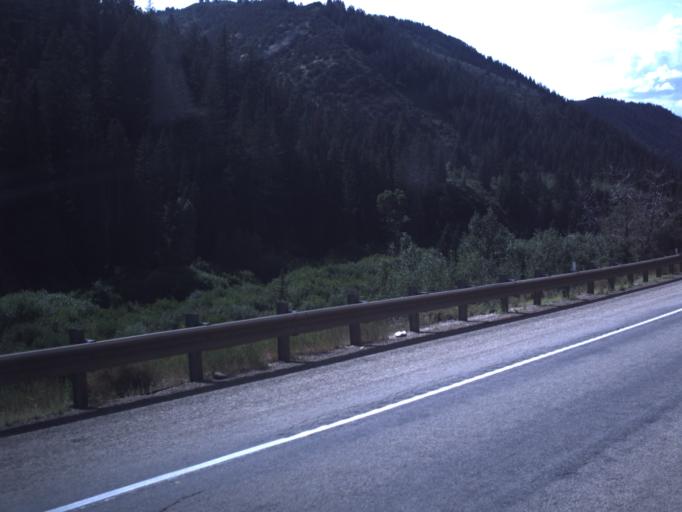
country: US
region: Utah
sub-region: Wasatch County
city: Heber
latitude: 40.3445
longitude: -111.2654
